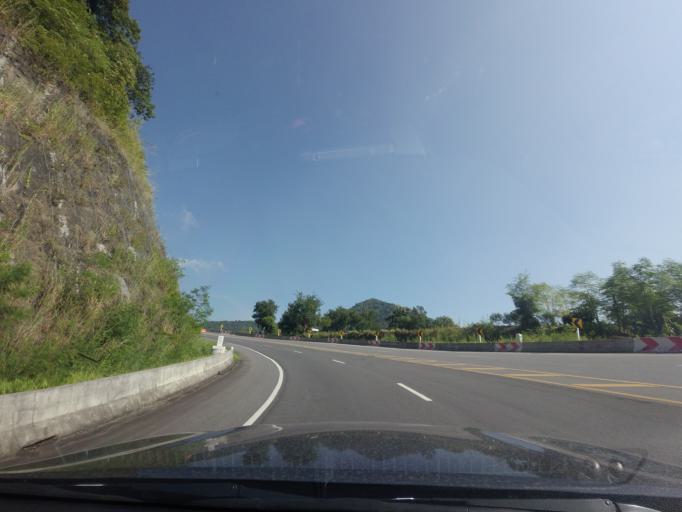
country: TH
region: Phetchabun
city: Lom Sak
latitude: 16.7814
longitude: 101.0985
